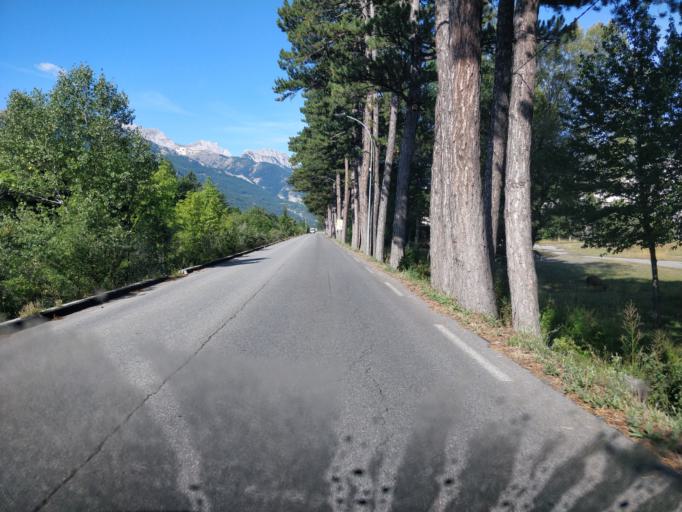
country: FR
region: Provence-Alpes-Cote d'Azur
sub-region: Departement des Alpes-de-Haute-Provence
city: Barcelonnette
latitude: 44.3864
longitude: 6.6392
